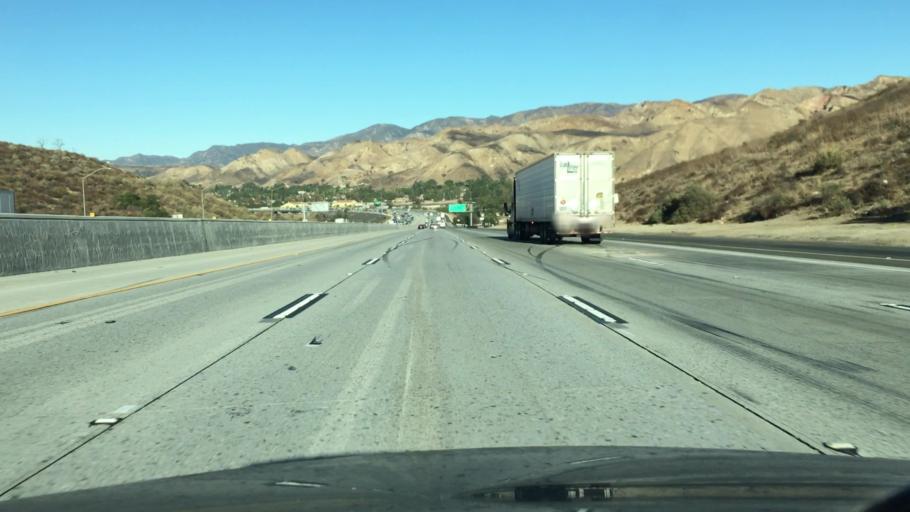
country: US
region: California
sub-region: Los Angeles County
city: Burbank
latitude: 34.2621
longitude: -118.3320
